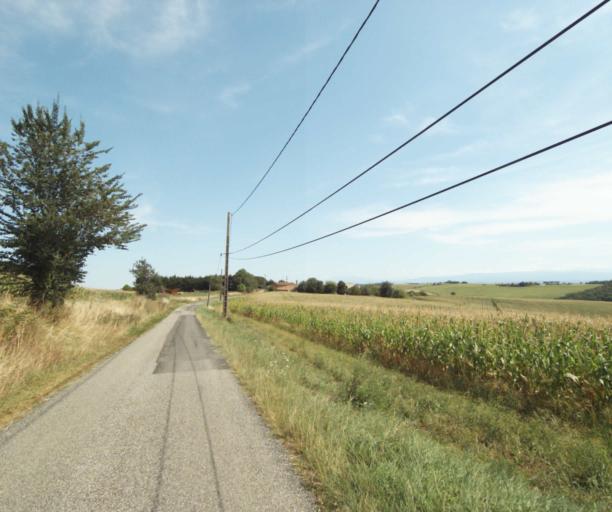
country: FR
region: Midi-Pyrenees
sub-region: Departement de la Haute-Garonne
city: Gaillac-Toulza
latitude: 43.2624
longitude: 1.4153
